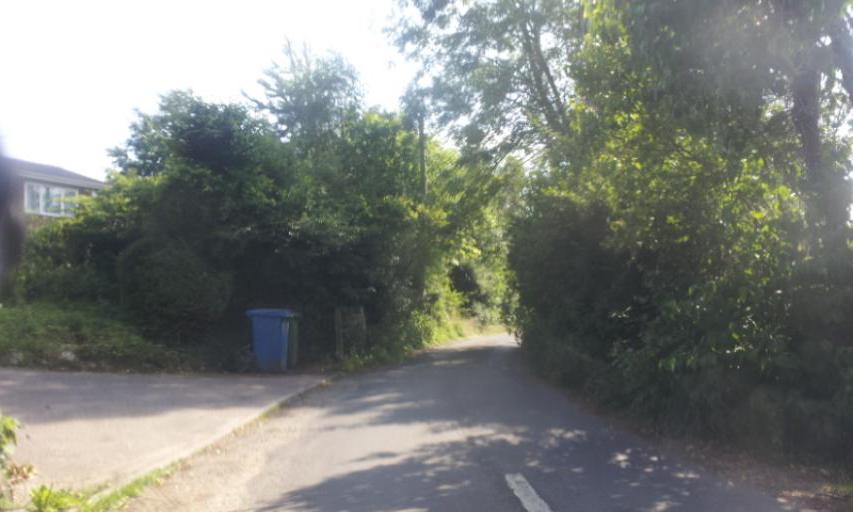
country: GB
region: England
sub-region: Kent
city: Teynham
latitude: 51.2810
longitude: 0.7706
